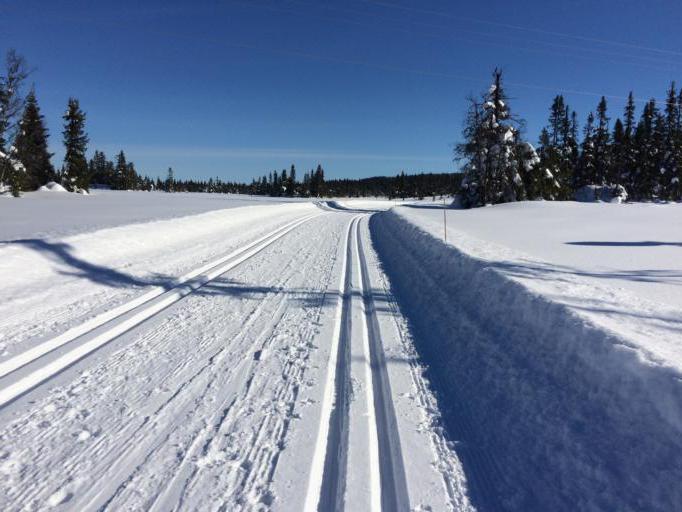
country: NO
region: Oppland
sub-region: Gausdal
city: Segalstad bru
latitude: 61.3268
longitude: 10.0829
